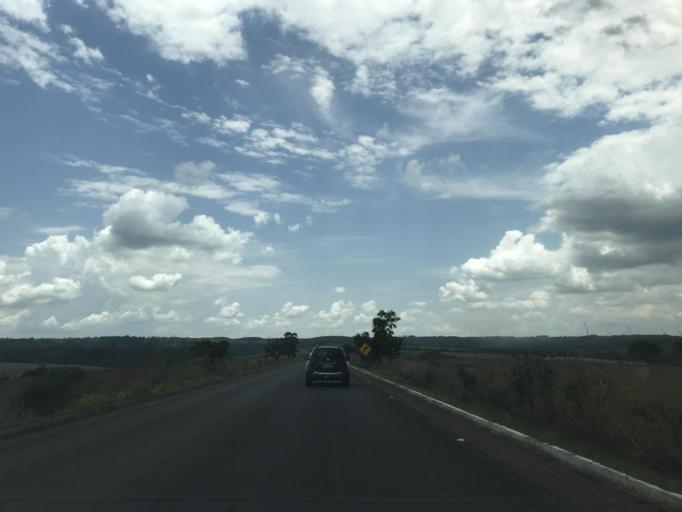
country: BR
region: Goias
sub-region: Vianopolis
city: Vianopolis
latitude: -16.9468
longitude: -48.5677
